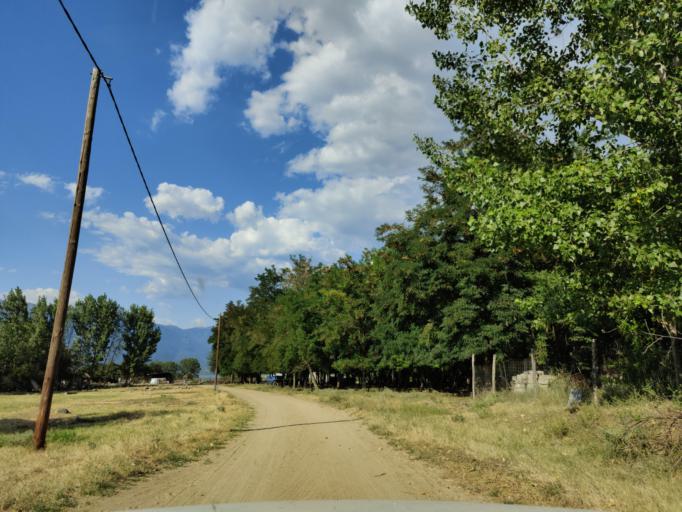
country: GR
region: Central Macedonia
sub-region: Nomos Serron
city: Chrysochorafa
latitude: 41.1825
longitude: 23.1064
